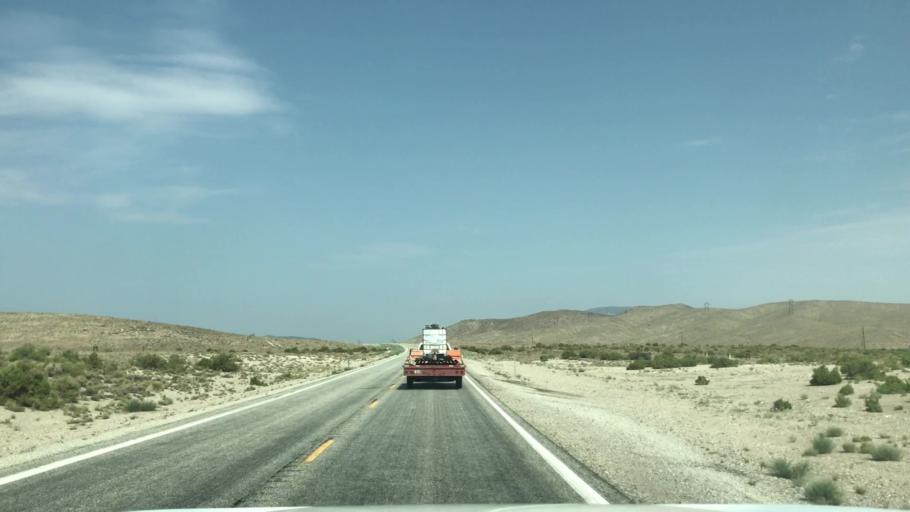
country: US
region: Nevada
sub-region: White Pine County
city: McGill
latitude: 39.0824
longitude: -114.1964
